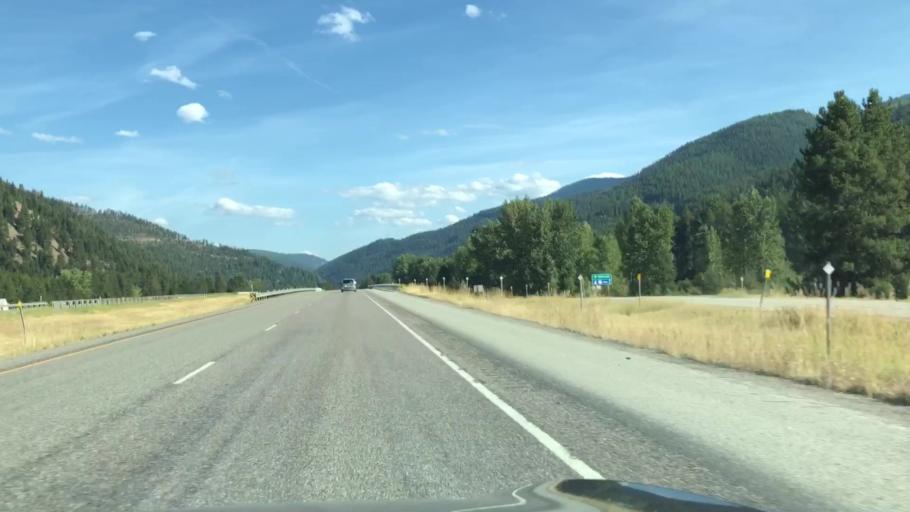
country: US
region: Montana
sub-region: Sanders County
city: Thompson Falls
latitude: 47.3762
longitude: -115.3541
